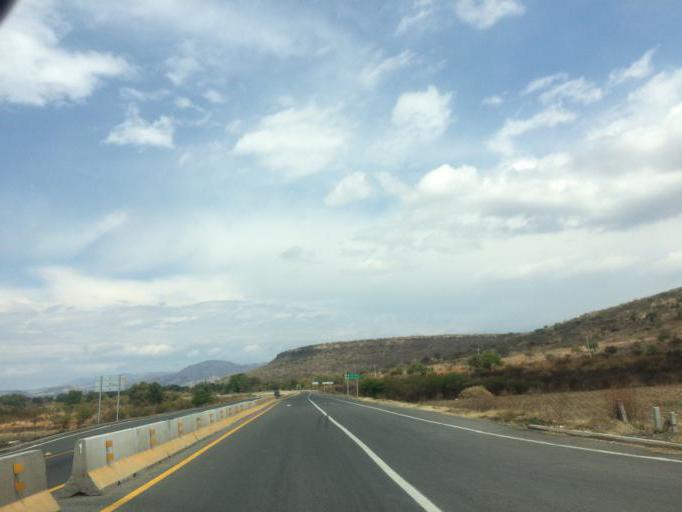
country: MX
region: Guanajuato
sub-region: Silao de la Victoria
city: Colonia Francisco Javier Mina
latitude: 21.0186
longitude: -101.4359
